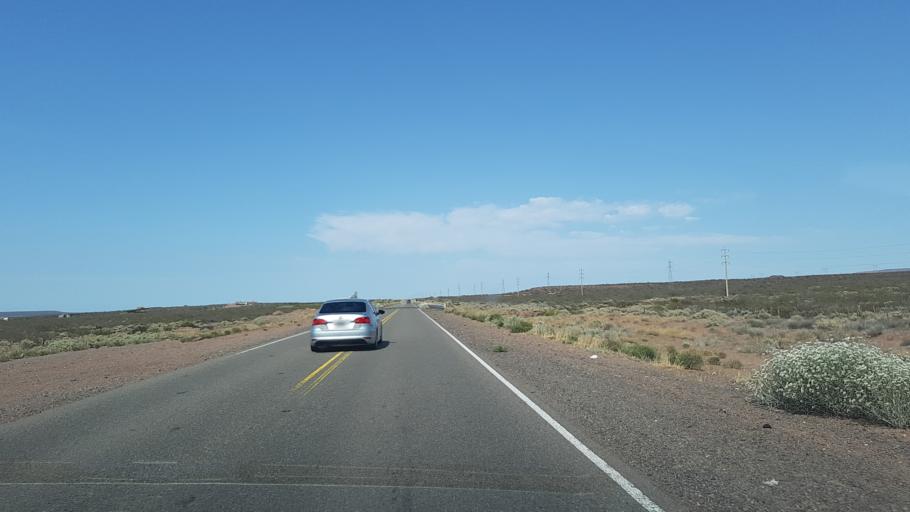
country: AR
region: Neuquen
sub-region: Departamento de Picun Leufu
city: Picun Leufu
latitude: -39.3286
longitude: -68.9657
